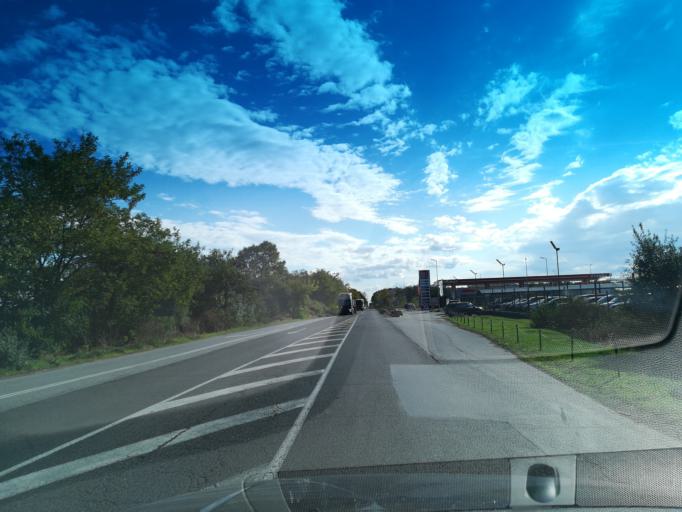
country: BG
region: Stara Zagora
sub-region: Obshtina Stara Zagora
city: Stara Zagora
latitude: 42.3572
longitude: 25.6569
